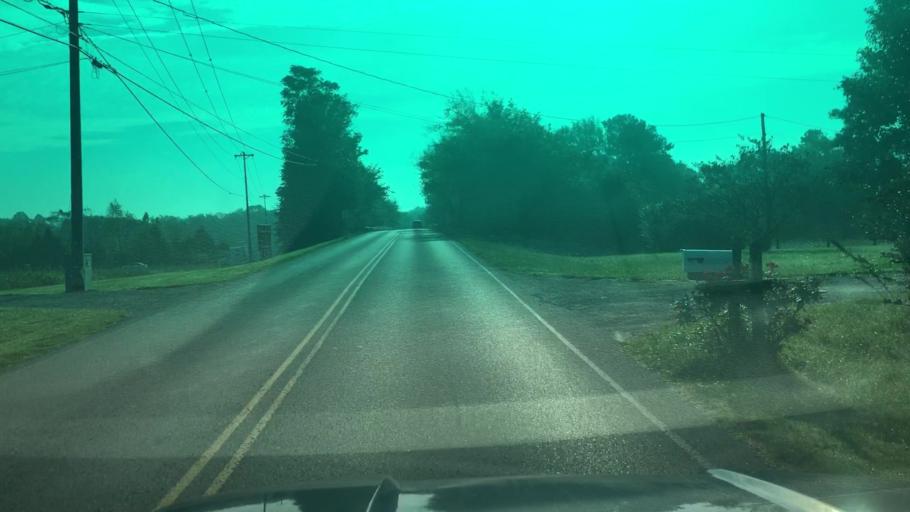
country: US
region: Tennessee
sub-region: Williamson County
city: Thompson's Station
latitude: 35.7899
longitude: -86.8629
